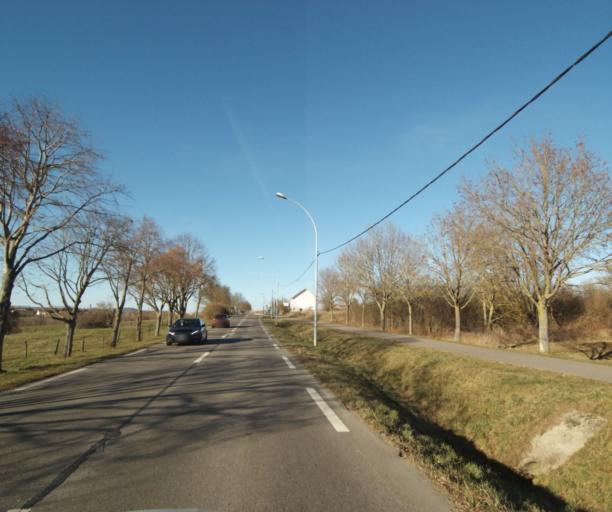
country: FR
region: Lorraine
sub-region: Departement de Meurthe-et-Moselle
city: Heillecourt
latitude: 48.6548
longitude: 6.2070
